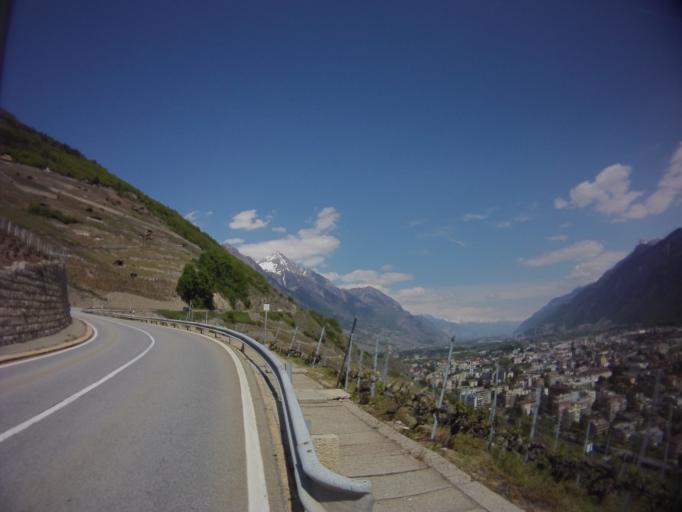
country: CH
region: Valais
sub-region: Martigny District
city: Martigny-Ville
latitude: 46.0969
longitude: 7.0594
